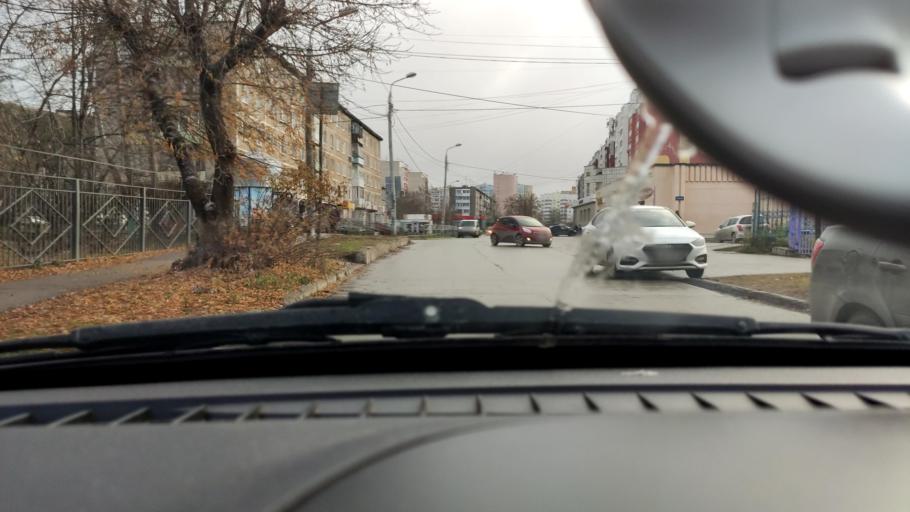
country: RU
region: Perm
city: Kondratovo
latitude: 58.0377
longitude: 56.1314
